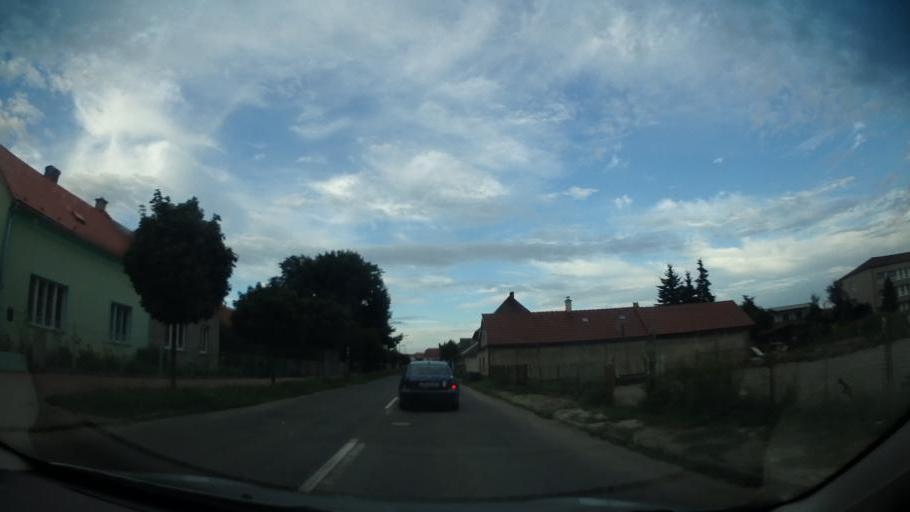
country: CZ
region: Olomoucky
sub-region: Okres Olomouc
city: Unicov
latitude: 49.7685
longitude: 17.1204
